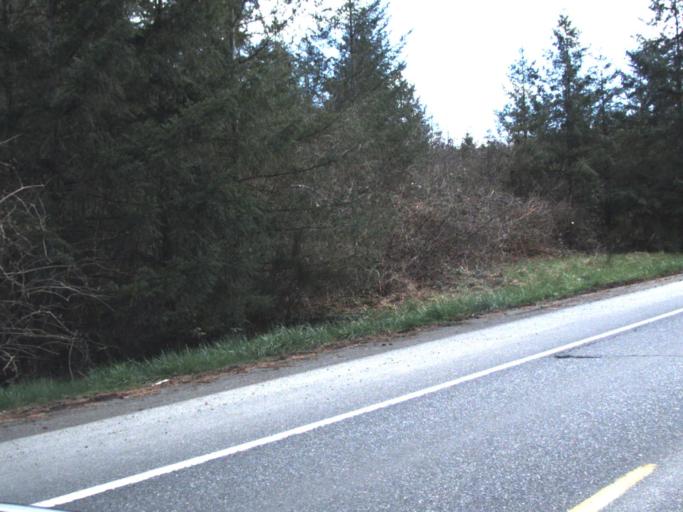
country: US
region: Washington
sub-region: King County
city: Black Diamond
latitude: 47.3370
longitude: -122.0148
